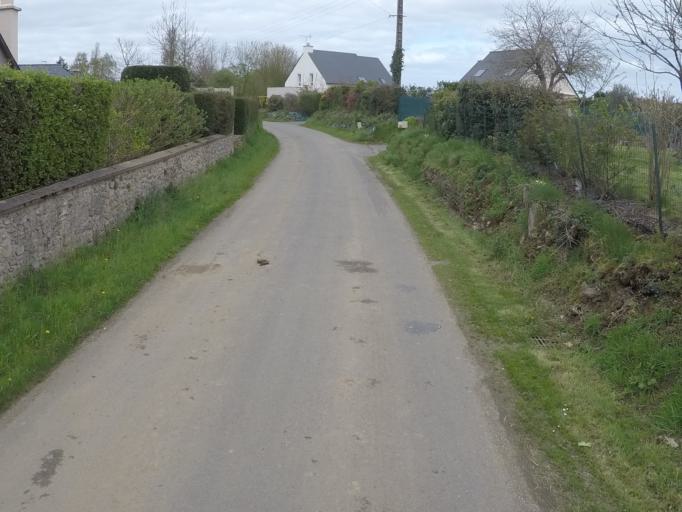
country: FR
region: Brittany
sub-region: Departement des Cotes-d'Armor
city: Lanvollon
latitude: 48.6379
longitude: -2.9679
